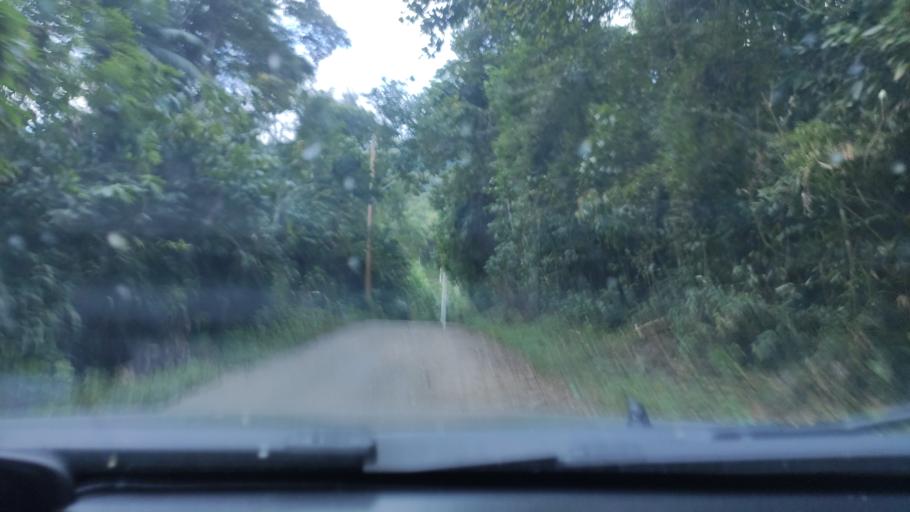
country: BR
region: Sao Paulo
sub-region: Sao Sebastiao
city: Sao Sebastiao
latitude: -23.7167
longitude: -45.4944
